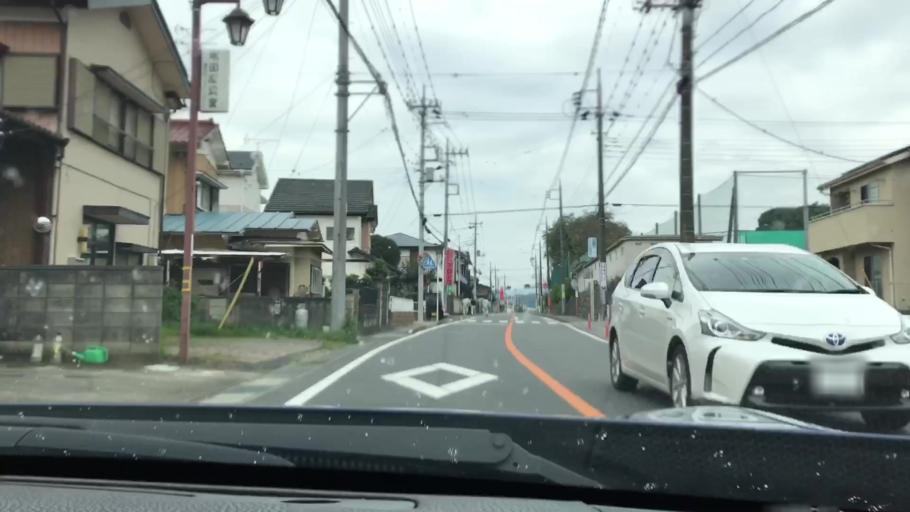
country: JP
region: Gunma
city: Kanekomachi
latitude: 36.3959
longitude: 138.9653
